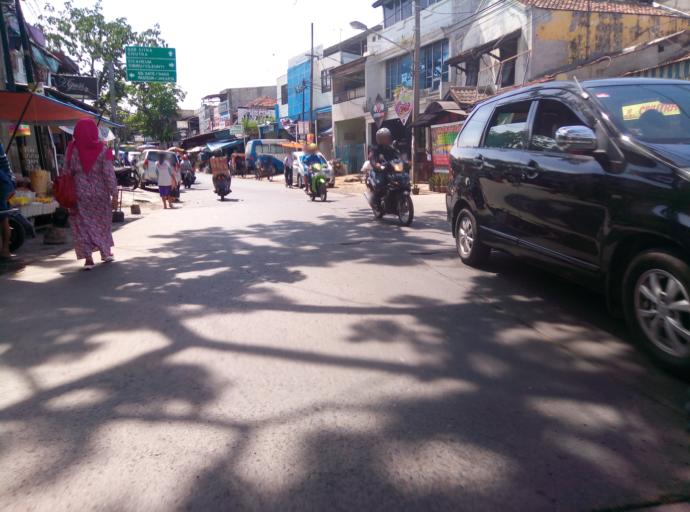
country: ID
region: West Java
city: Bandung
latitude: -6.9015
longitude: 107.6441
